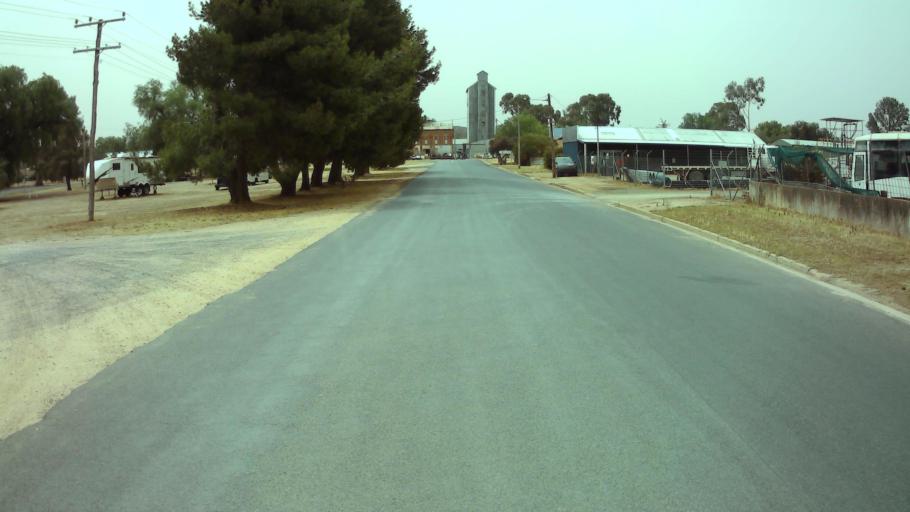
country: AU
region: New South Wales
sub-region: Weddin
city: Grenfell
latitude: -33.8965
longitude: 148.1559
